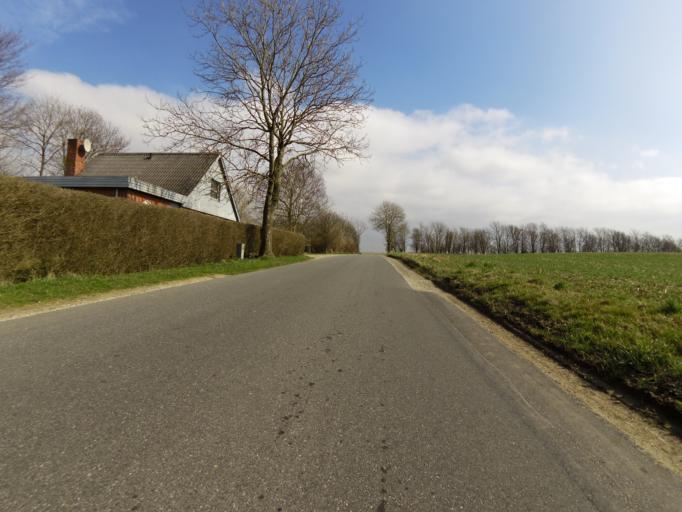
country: DK
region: Central Jutland
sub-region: Holstebro Kommune
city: Holstebro
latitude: 56.4380
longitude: 8.6584
